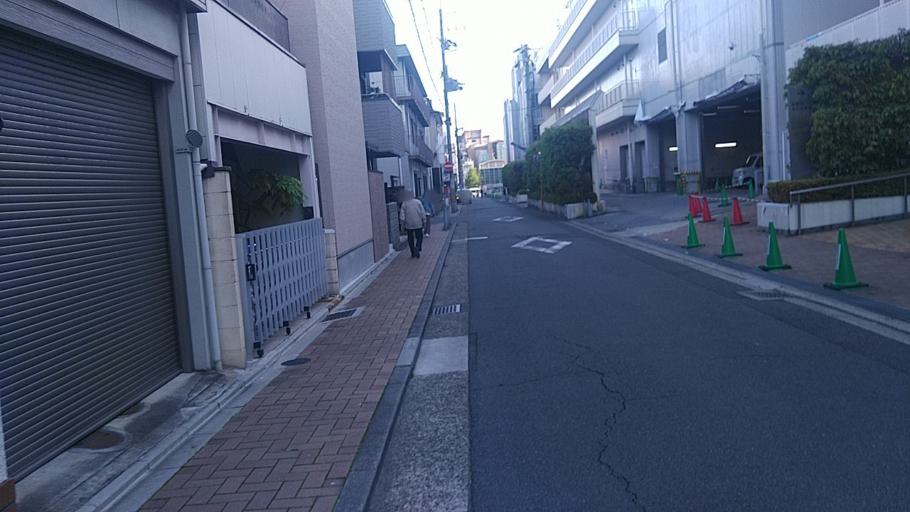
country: JP
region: Kyoto
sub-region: Kyoto-shi
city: Kamigyo-ku
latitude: 35.0458
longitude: 135.7588
